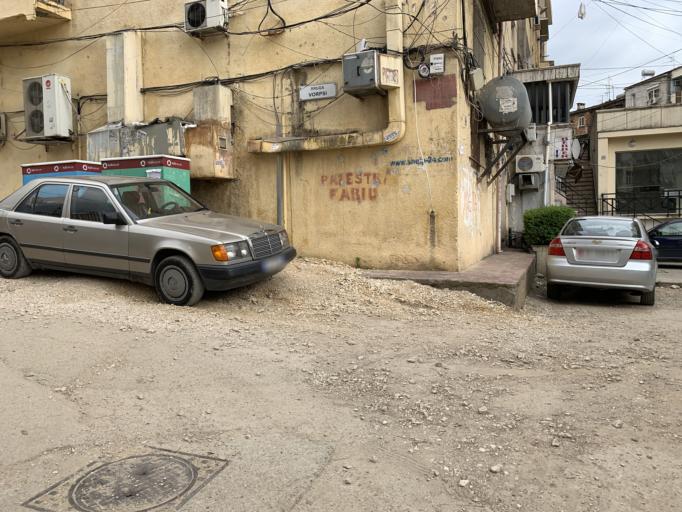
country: AL
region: Tirane
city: Tirana
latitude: 41.3302
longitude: 19.8152
